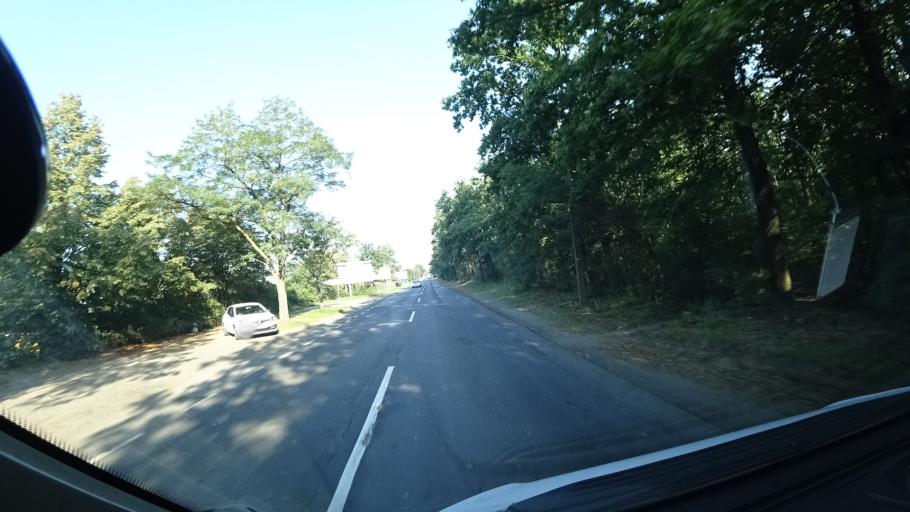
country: PL
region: Opole Voivodeship
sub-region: Powiat kedzierzynsko-kozielski
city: Kedzierzyn-Kozle
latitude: 50.3301
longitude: 18.1980
